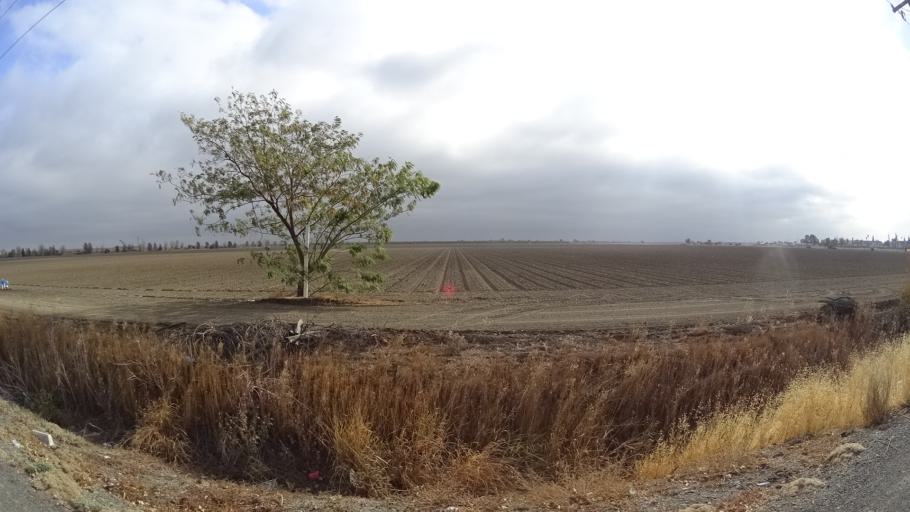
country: US
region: California
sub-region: Yolo County
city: Esparto
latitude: 38.7001
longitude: -122.0150
